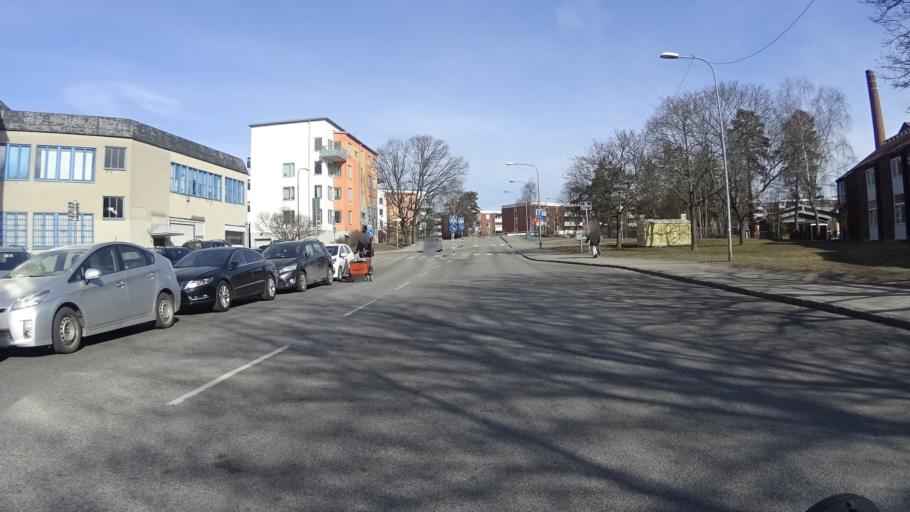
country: SE
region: Stockholm
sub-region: Nacka Kommun
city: Nacka
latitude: 59.2795
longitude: 18.1271
